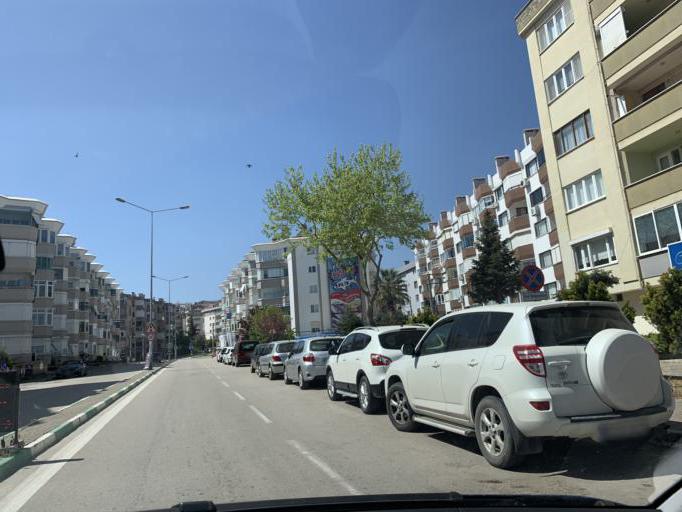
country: TR
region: Bursa
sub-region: Mudanya
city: Mudanya
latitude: 40.3555
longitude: 28.9264
